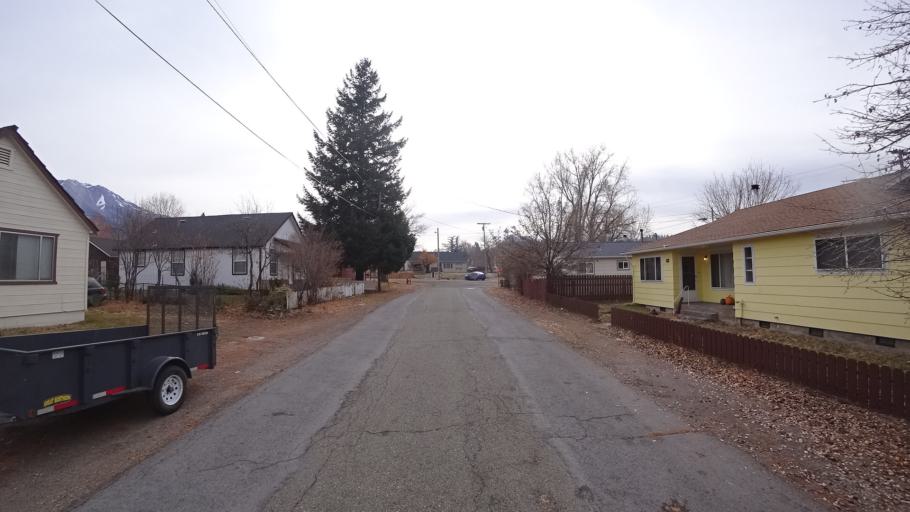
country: US
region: California
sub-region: Siskiyou County
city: Weed
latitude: 41.4316
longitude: -122.3765
